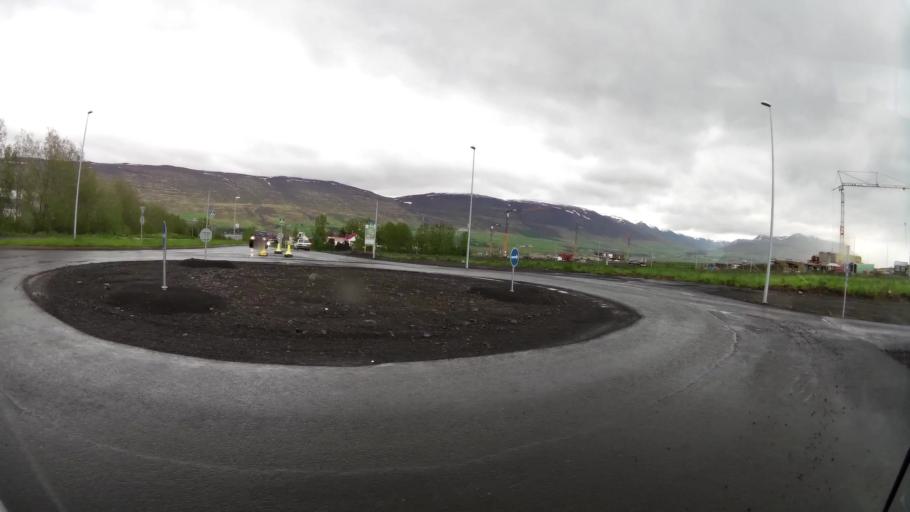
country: IS
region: Northeast
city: Akureyri
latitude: 65.6613
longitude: -18.0987
